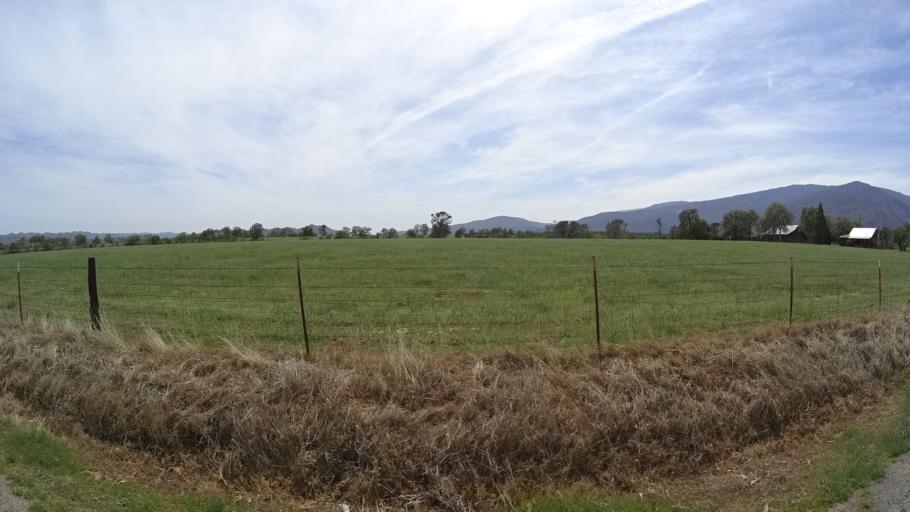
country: US
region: California
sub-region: Glenn County
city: Willows
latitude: 39.5843
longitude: -122.5863
